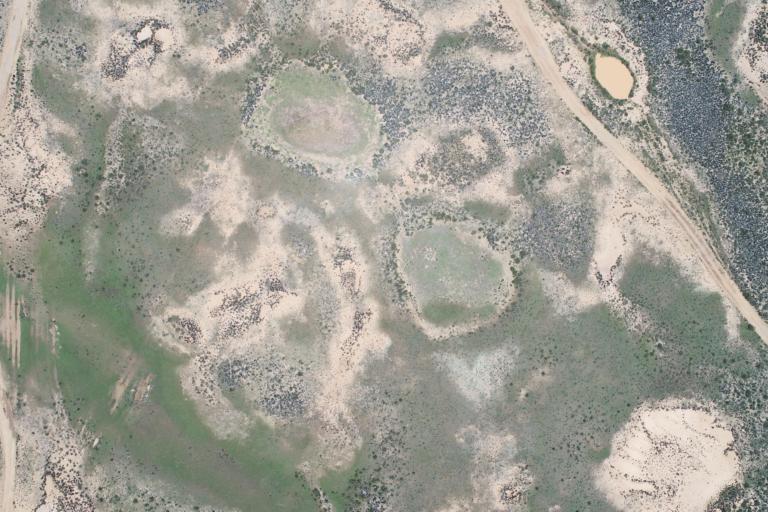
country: BO
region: La Paz
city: Patacamaya
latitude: -17.2818
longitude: -68.5050
